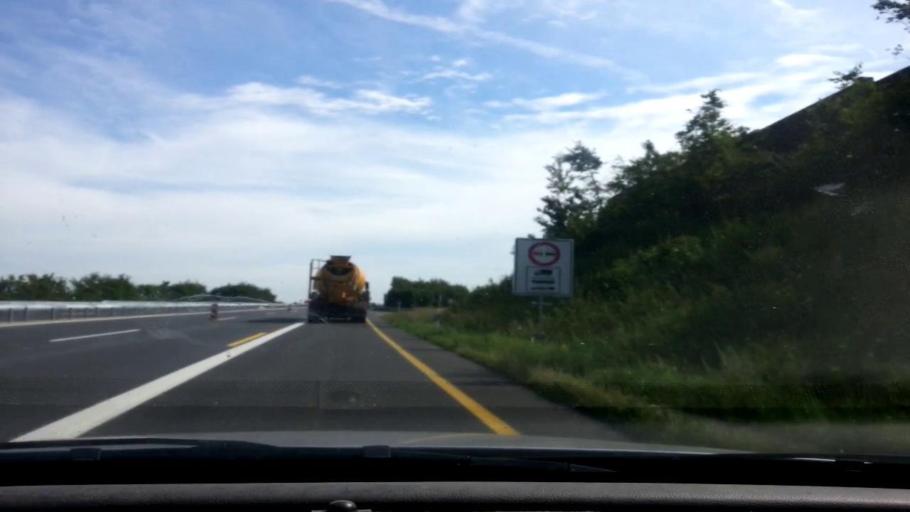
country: DE
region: Bavaria
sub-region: Upper Franconia
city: Memmelsdorf
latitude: 49.9509
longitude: 10.9734
